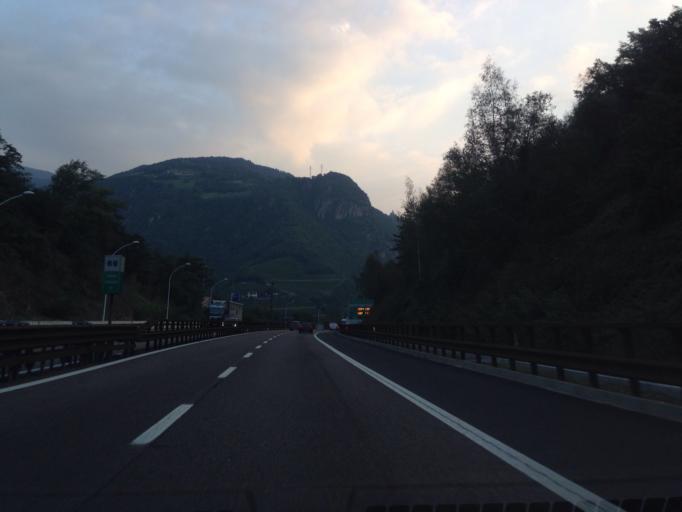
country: IT
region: Trentino-Alto Adige
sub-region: Bolzano
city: Fie Allo Sciliar
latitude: 46.5293
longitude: 11.4907
